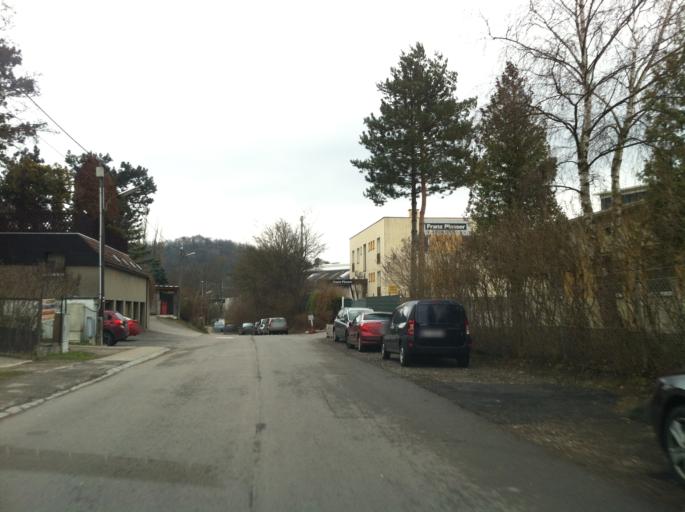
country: AT
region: Lower Austria
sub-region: Politischer Bezirk Wien-Umgebung
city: Purkersdorf
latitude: 48.2077
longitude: 16.1975
